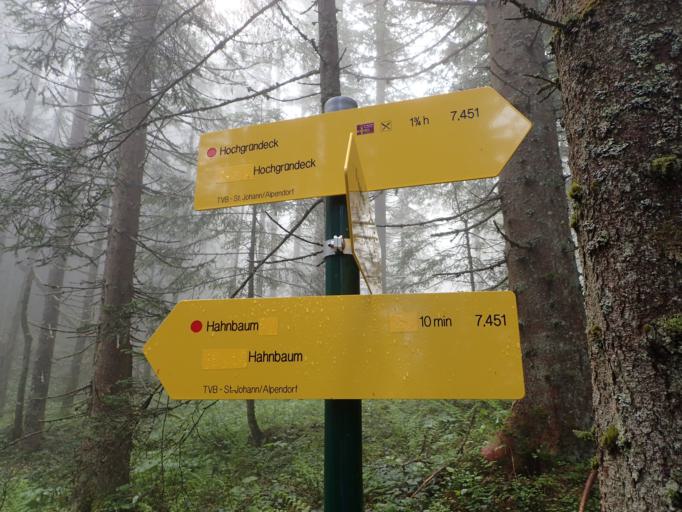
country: AT
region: Salzburg
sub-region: Politischer Bezirk Sankt Johann im Pongau
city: Sankt Johann im Pongau
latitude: 47.3425
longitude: 13.2276
